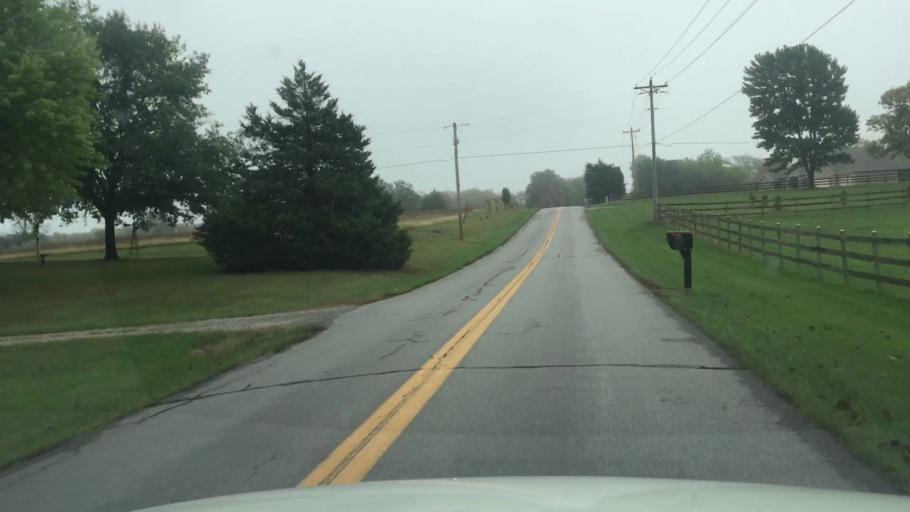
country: US
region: Missouri
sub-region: Boone County
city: Columbia
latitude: 38.8568
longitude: -92.3120
